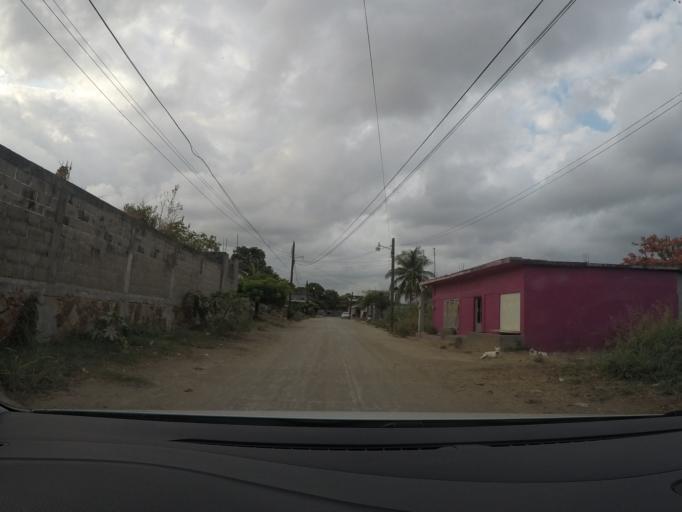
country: MX
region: Oaxaca
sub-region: Salina Cruz
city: Salina Cruz
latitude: 16.2117
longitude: -95.1974
